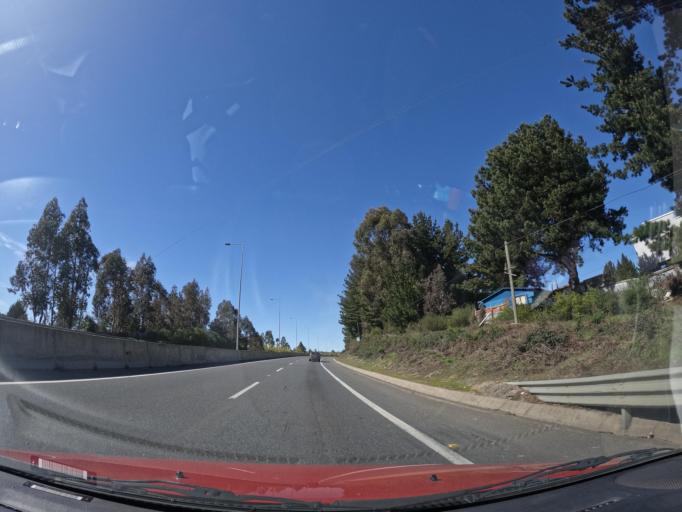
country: CL
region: Biobio
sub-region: Provincia de Concepcion
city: Chiguayante
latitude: -36.9043
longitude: -72.7899
